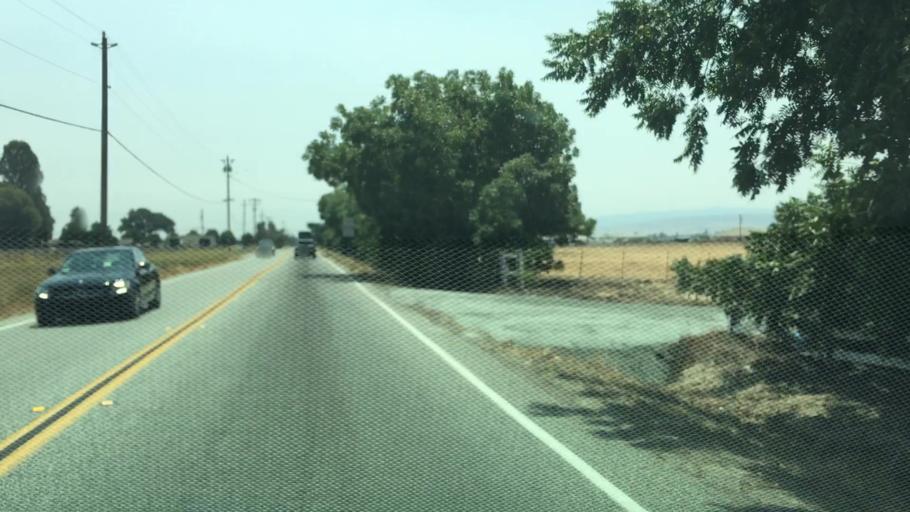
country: US
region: California
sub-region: Santa Clara County
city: Gilroy
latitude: 37.0297
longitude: -121.5289
